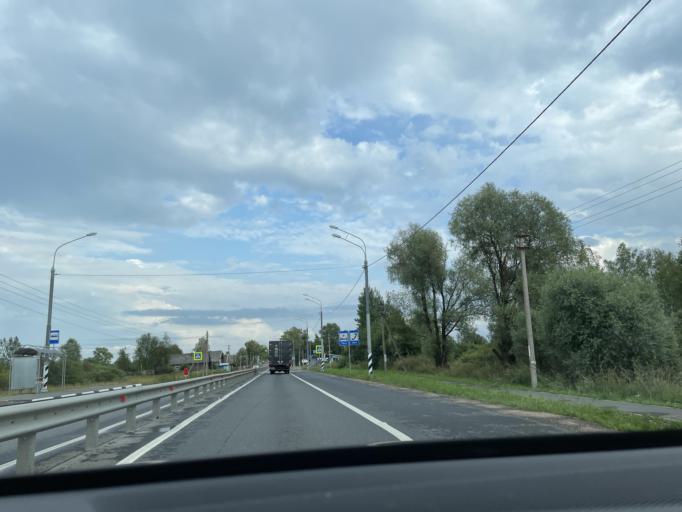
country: RU
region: Tverskaya
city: Kuzhenkino
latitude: 57.7273
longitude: 34.0653
